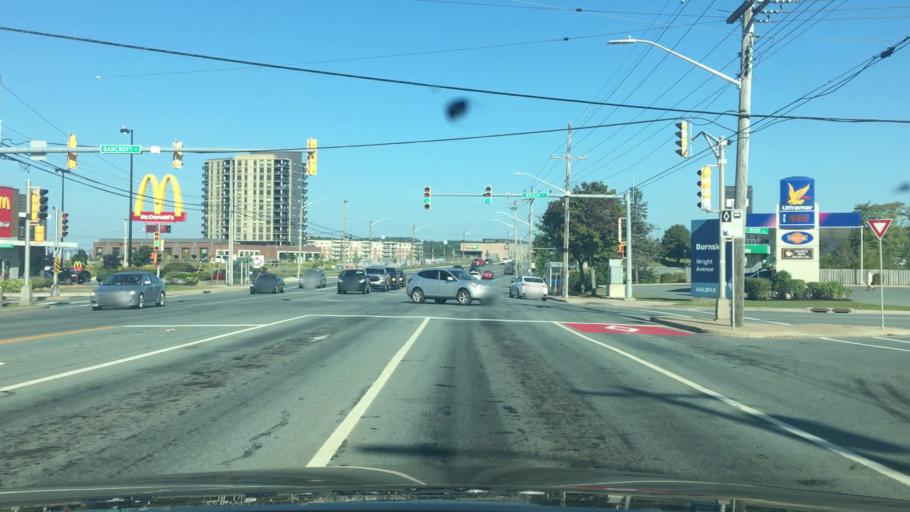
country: CA
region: Nova Scotia
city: Dartmouth
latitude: 44.6981
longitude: -63.6045
